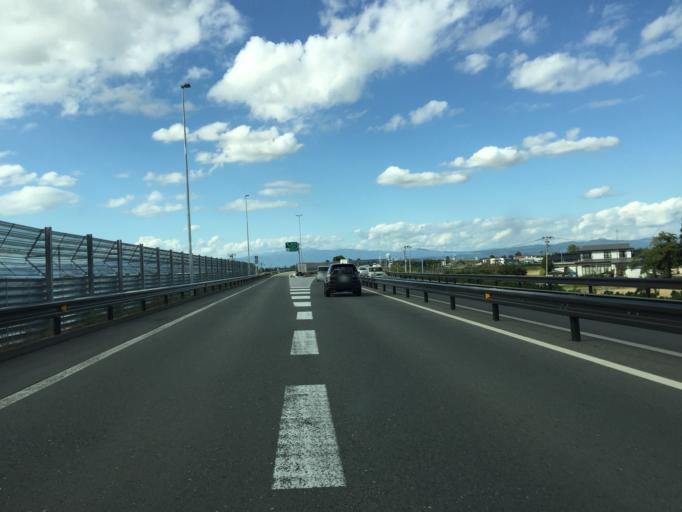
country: JP
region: Yamagata
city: Yonezawa
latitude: 37.9170
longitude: 140.1372
